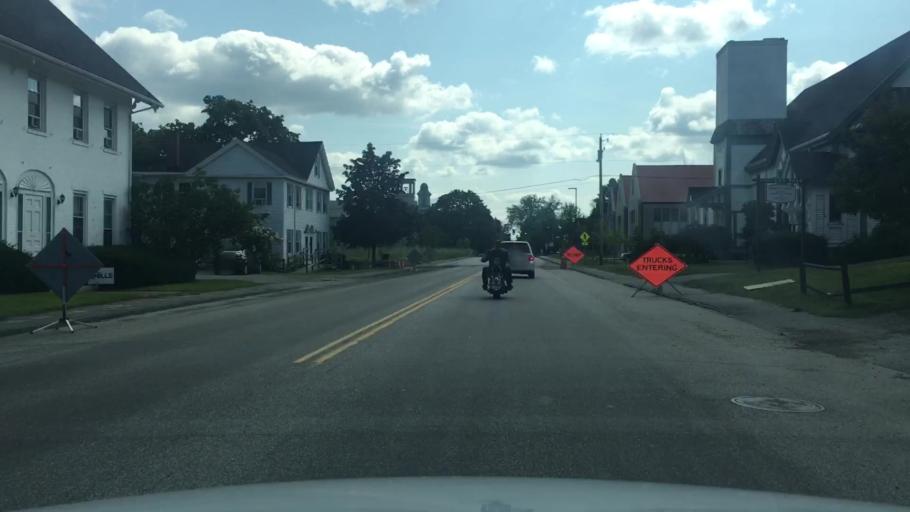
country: US
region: Maine
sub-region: Kennebec County
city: Augusta
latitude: 44.3169
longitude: -69.7768
